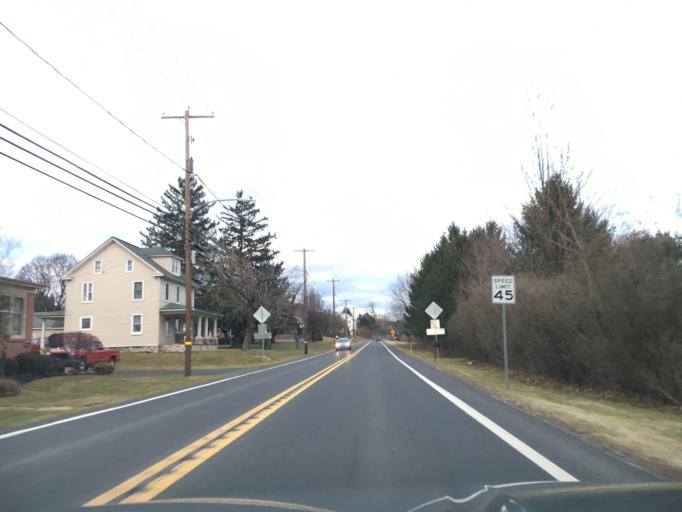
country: US
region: Pennsylvania
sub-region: Lehigh County
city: Schnecksville
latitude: 40.6837
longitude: -75.6903
